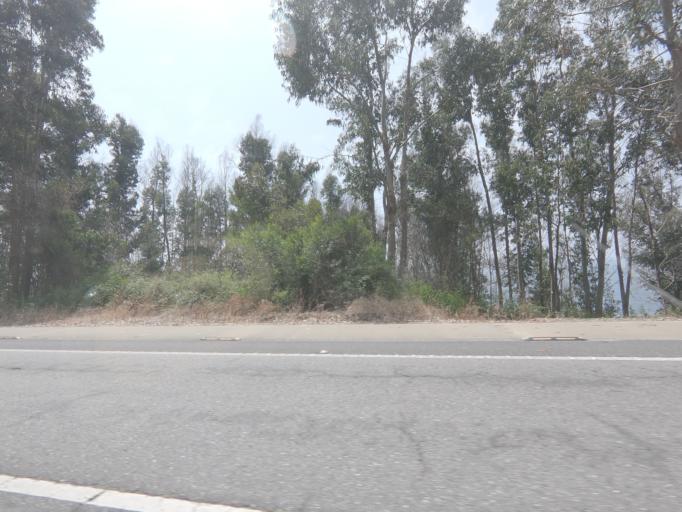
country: ES
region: Galicia
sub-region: Provincia de Pontevedra
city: A Guarda
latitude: 41.9309
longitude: -8.8820
